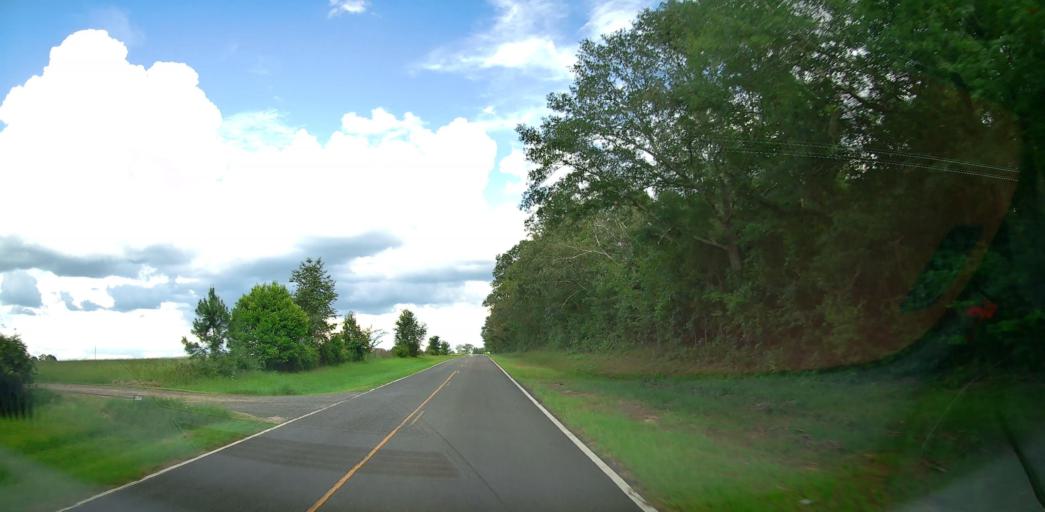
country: US
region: Georgia
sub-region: Bleckley County
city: Cochran
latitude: 32.4115
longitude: -83.4343
